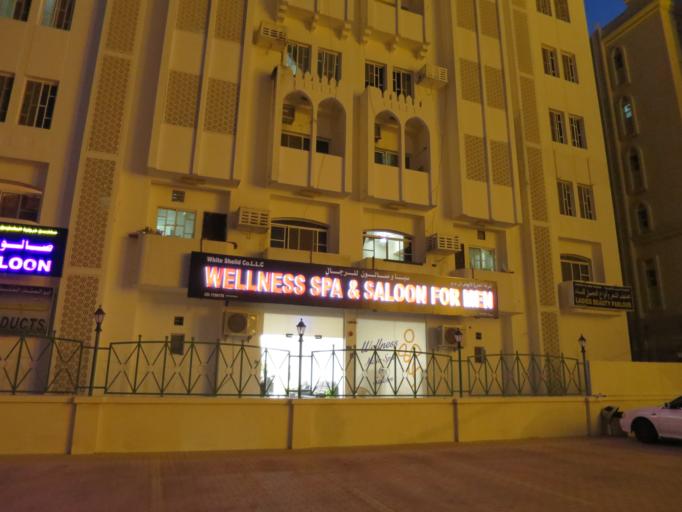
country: OM
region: Muhafazat Masqat
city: Bawshar
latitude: 23.5861
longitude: 58.4255
